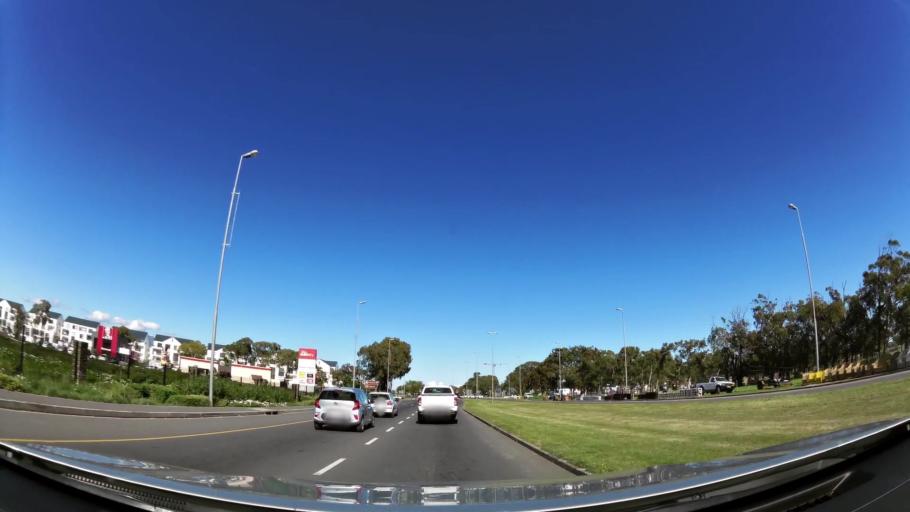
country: ZA
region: Western Cape
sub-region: Cape Winelands District Municipality
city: Stellenbosch
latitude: -34.0886
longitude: 18.8197
